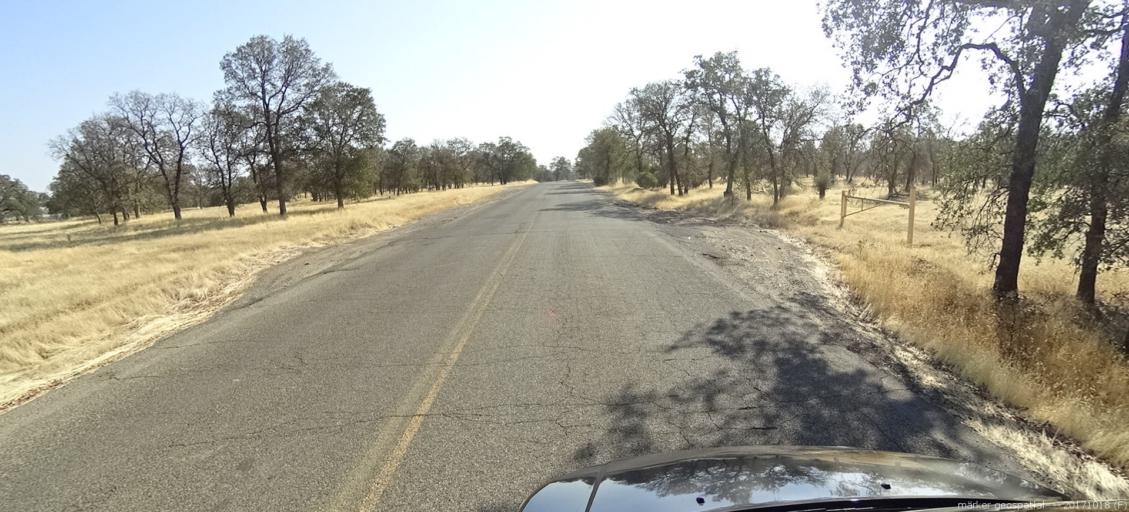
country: US
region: California
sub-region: Shasta County
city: Palo Cedro
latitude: 40.5587
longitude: -122.3009
